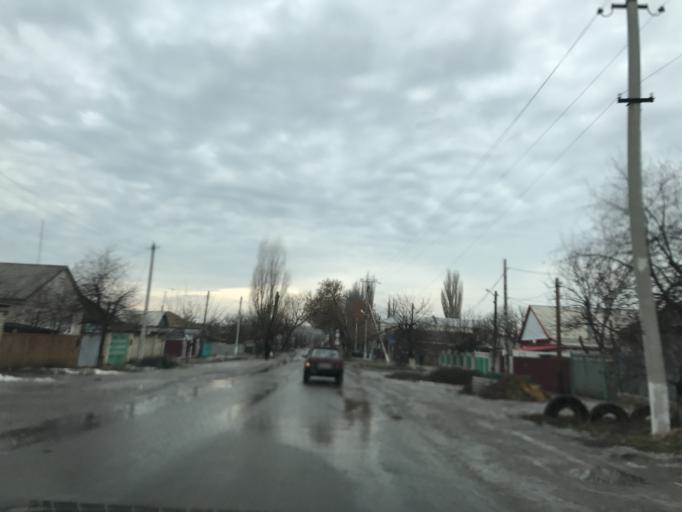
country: RU
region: Rostov
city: Glubokiy
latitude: 48.5223
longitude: 40.3157
